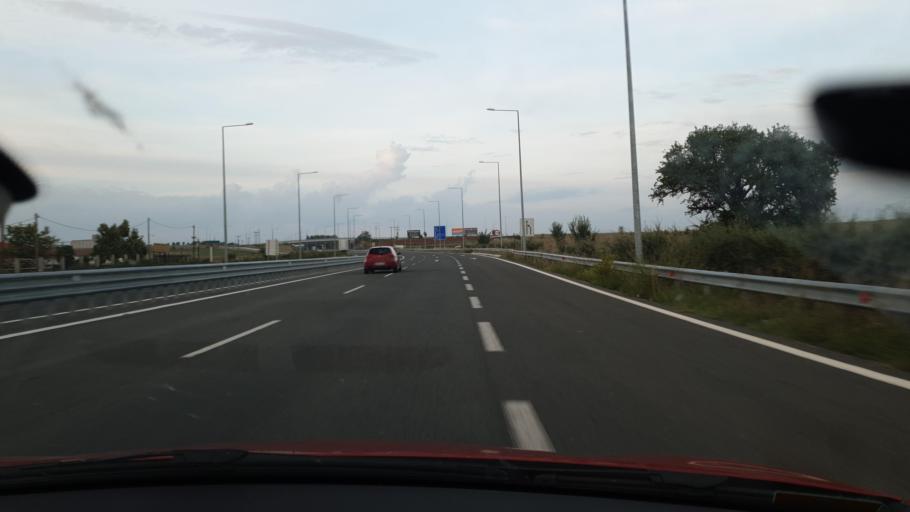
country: GR
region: Central Macedonia
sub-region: Nomos Kilkis
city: Kristoni
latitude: 40.9566
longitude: 22.8493
